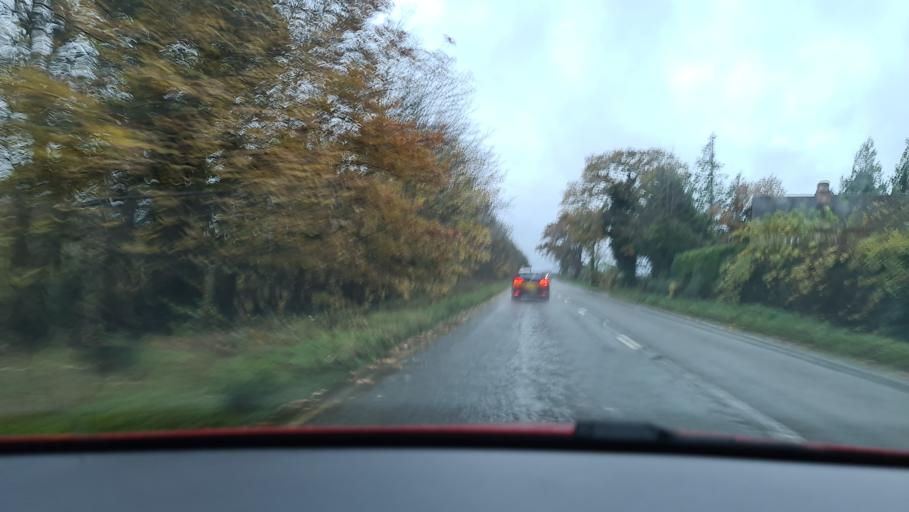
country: GB
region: England
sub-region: Oxfordshire
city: Somerton
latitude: 51.9309
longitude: -1.2172
